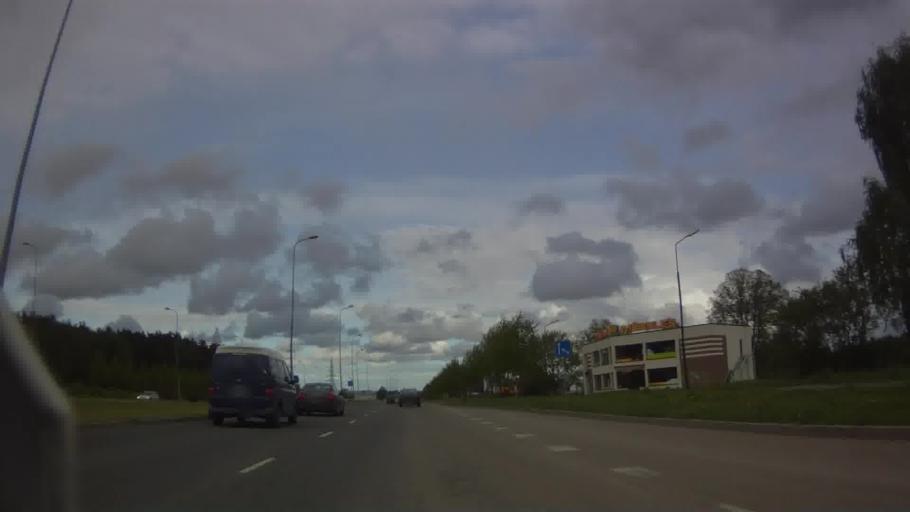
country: LV
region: Stopini
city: Ulbroka
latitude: 56.9537
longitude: 24.2099
